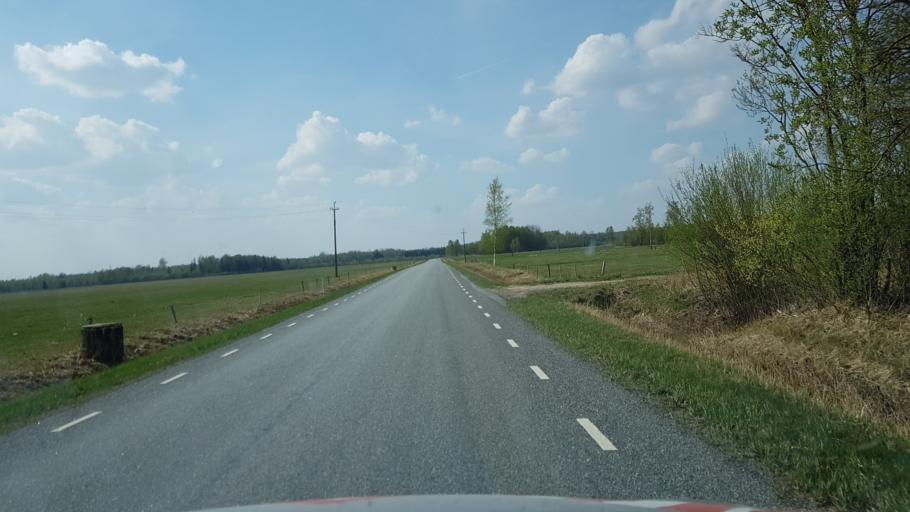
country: EE
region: Paernumaa
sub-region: Sindi linn
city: Sindi
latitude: 58.4321
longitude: 24.6351
